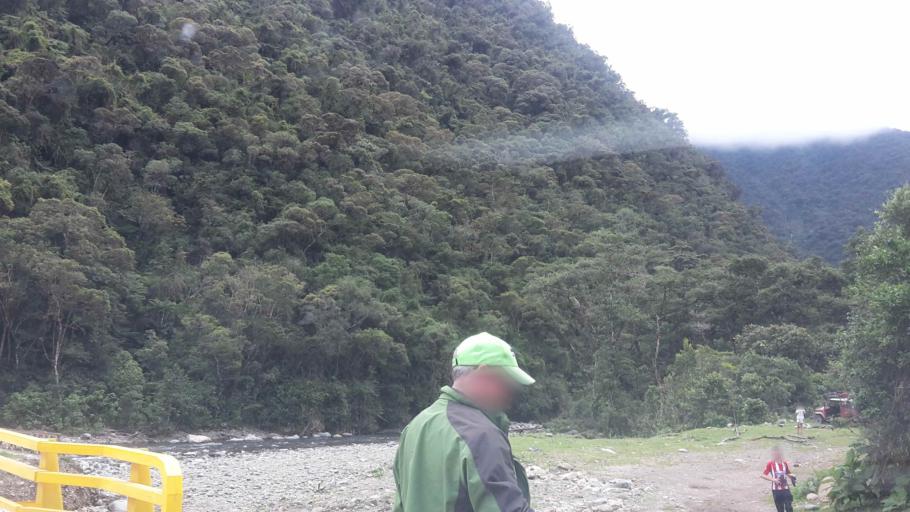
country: BO
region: Cochabamba
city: Totora
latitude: -17.4962
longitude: -65.2731
